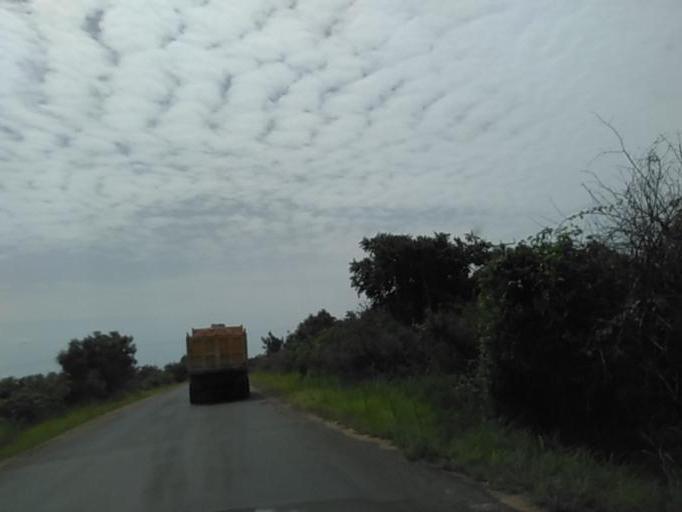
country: GH
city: Akropong
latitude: 6.0953
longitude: 0.0546
